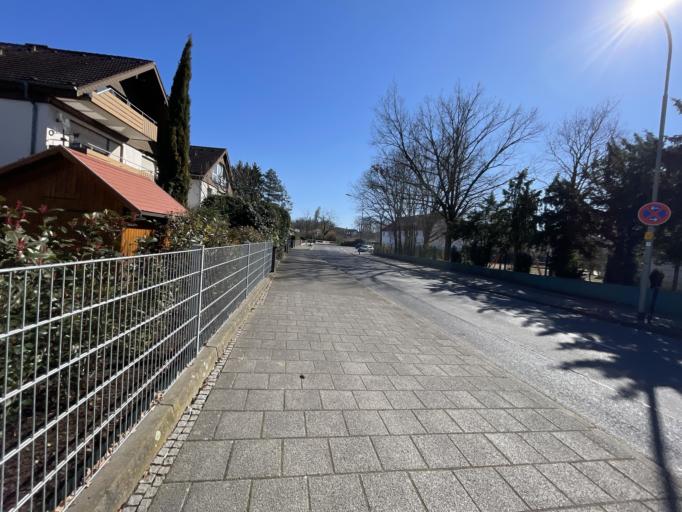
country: DE
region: Hesse
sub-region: Regierungsbezirk Darmstadt
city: Offenbach
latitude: 50.0845
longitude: 8.7599
